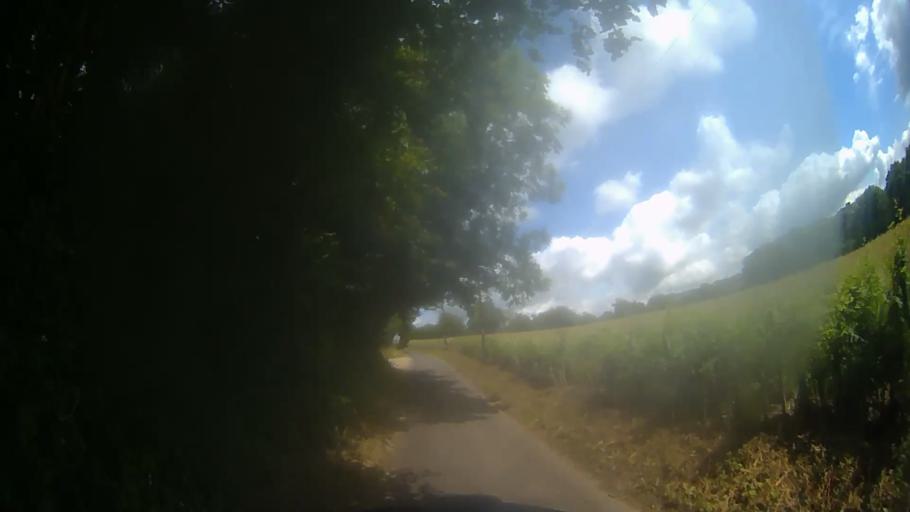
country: GB
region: England
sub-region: Hampshire
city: Andover
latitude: 51.2569
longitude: -1.4341
